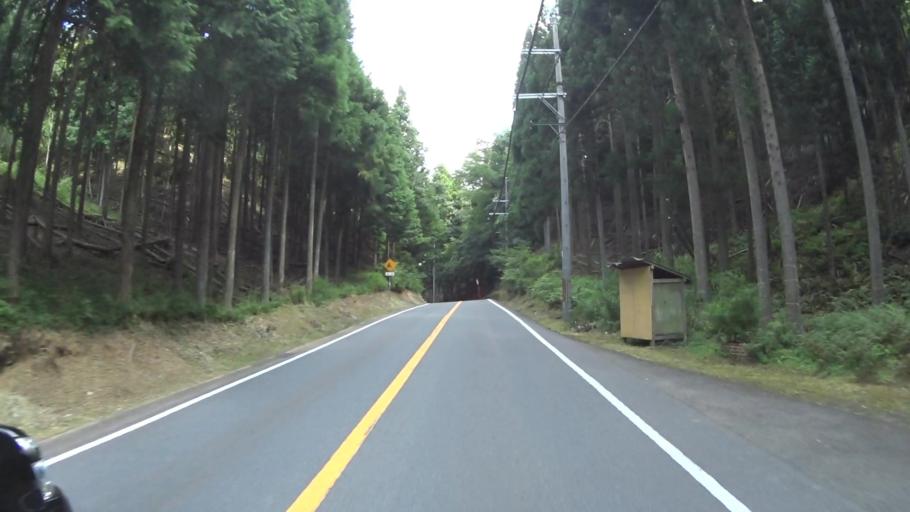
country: JP
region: Kyoto
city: Kameoka
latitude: 35.2764
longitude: 135.5701
